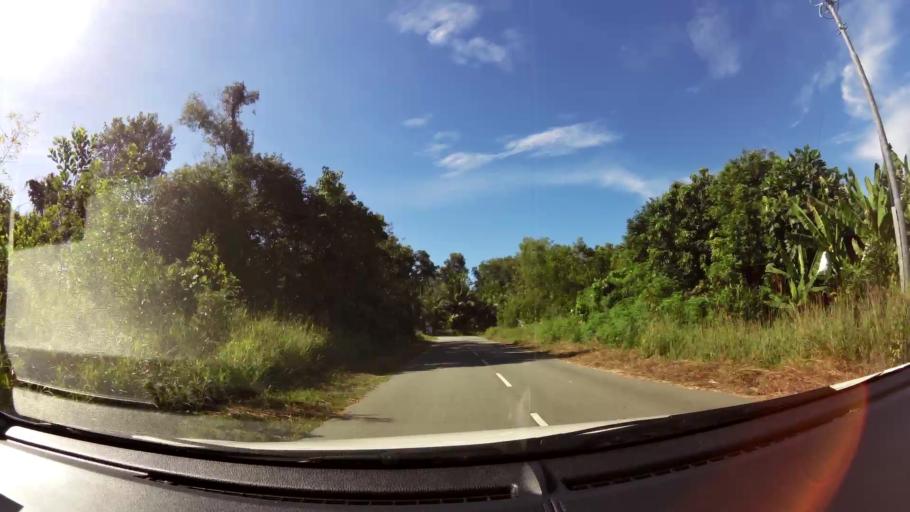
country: BN
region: Brunei and Muara
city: Bandar Seri Begawan
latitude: 4.9658
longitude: 114.9309
